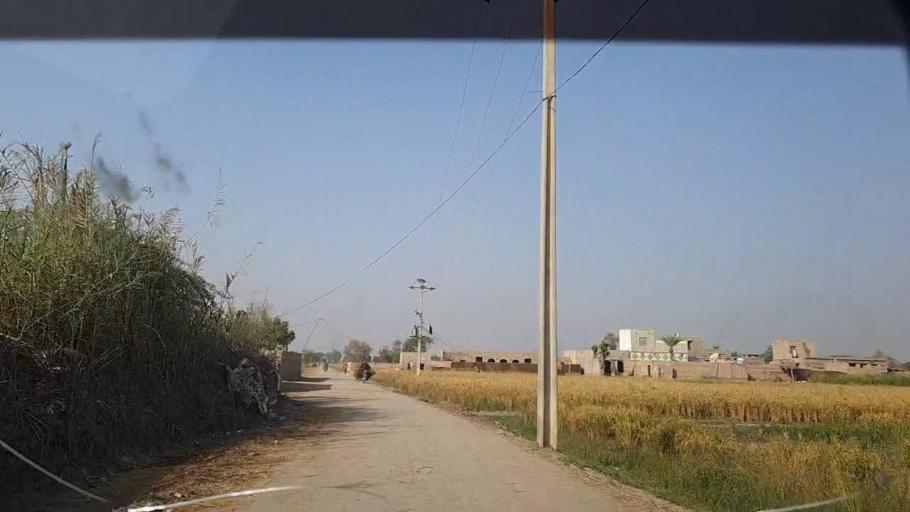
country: PK
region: Sindh
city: Shikarpur
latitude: 28.1179
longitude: 68.5835
